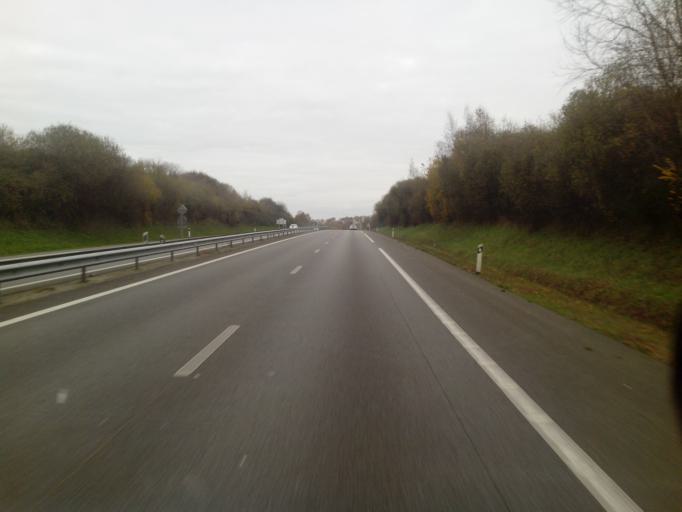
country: FR
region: Brittany
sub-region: Departement d'Ille-et-Vilaine
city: La Dominelais
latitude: 47.7521
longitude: -1.7152
